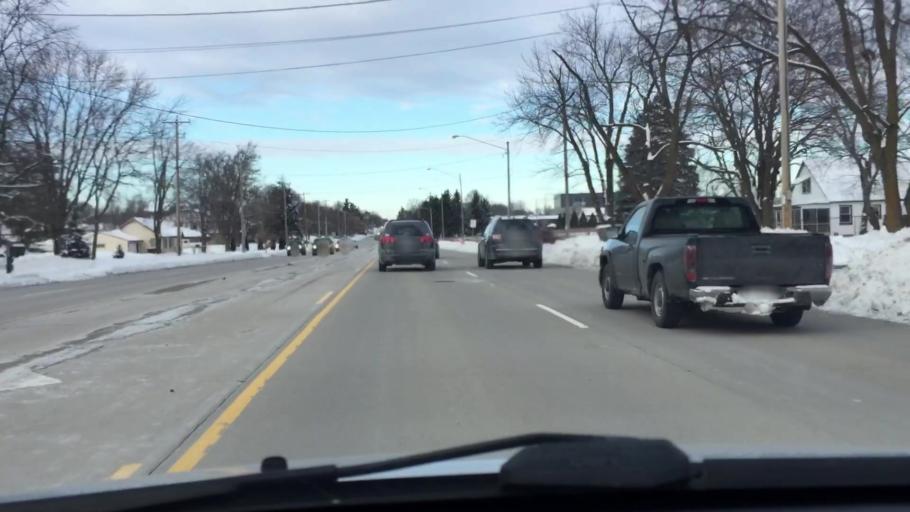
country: US
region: Wisconsin
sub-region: Waukesha County
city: Sussex
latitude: 43.1235
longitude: -88.2097
